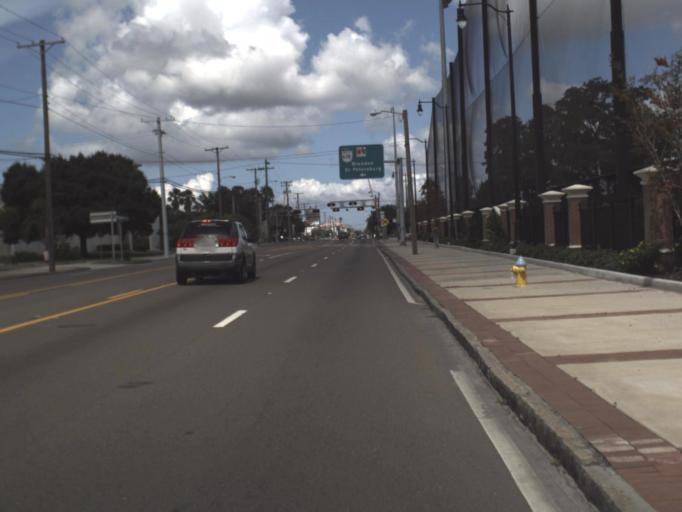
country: US
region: Florida
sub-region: Hillsborough County
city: Tampa
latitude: 27.9447
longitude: -82.4708
